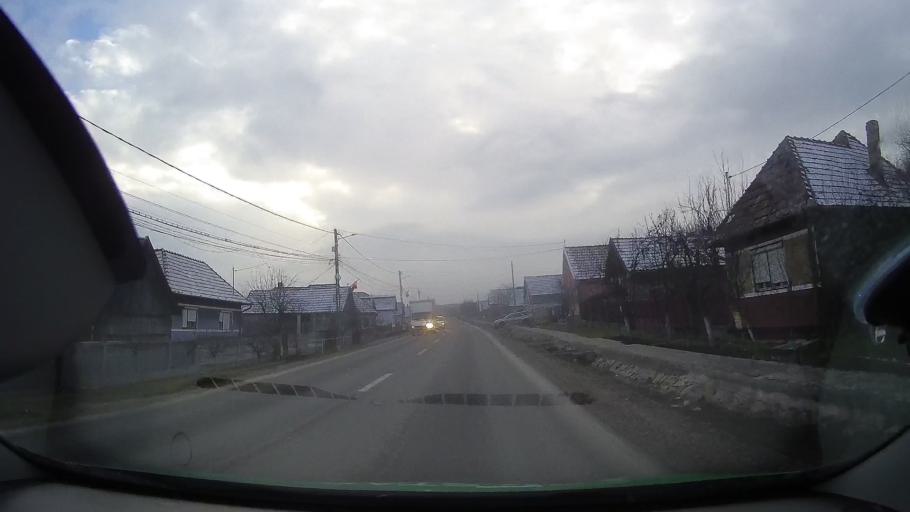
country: RO
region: Mures
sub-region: Comuna Cucerdea
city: Cucerdea
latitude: 46.3977
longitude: 24.2600
